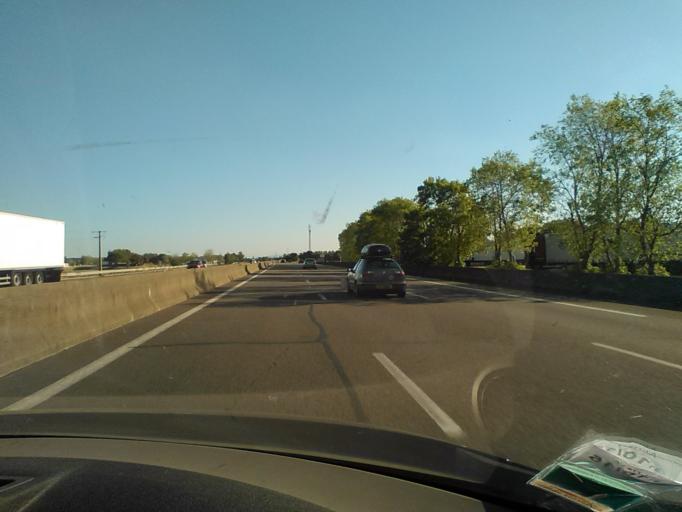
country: FR
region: Rhone-Alpes
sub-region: Departement de l'Ain
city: Guereins
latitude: 46.1432
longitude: 4.7668
